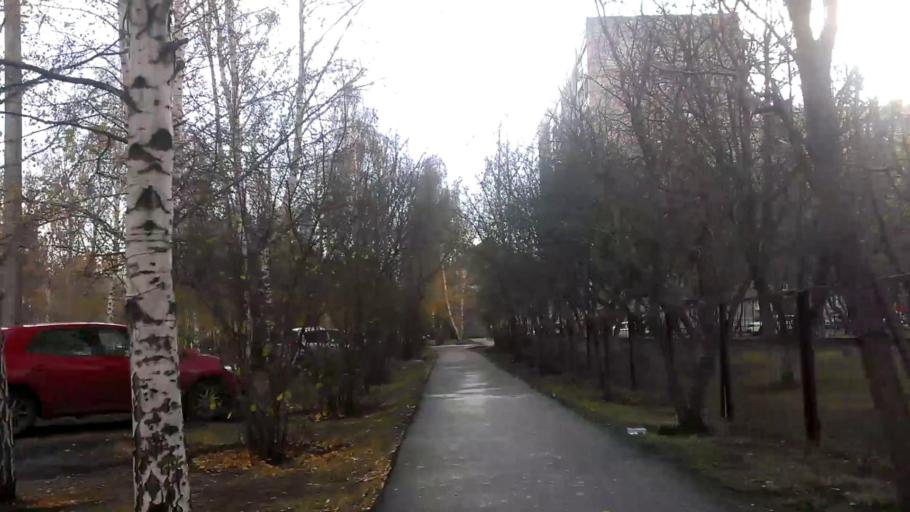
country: RU
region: Altai Krai
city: Novosilikatnyy
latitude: 53.3572
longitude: 83.6781
